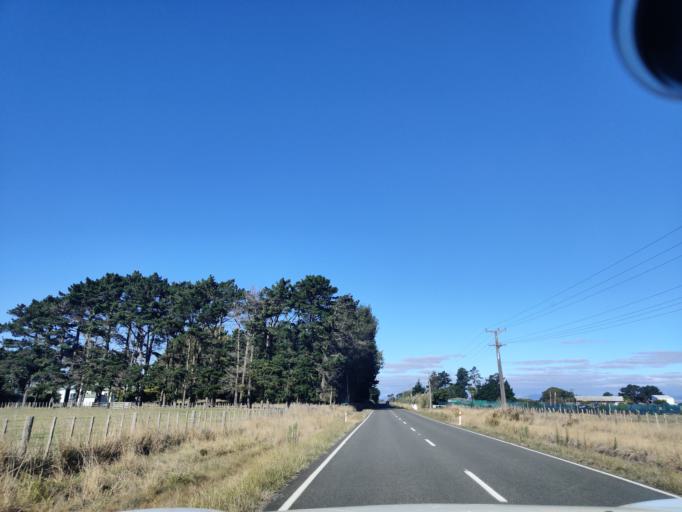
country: NZ
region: Manawatu-Wanganui
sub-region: Horowhenua District
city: Foxton
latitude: -40.3861
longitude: 175.2889
